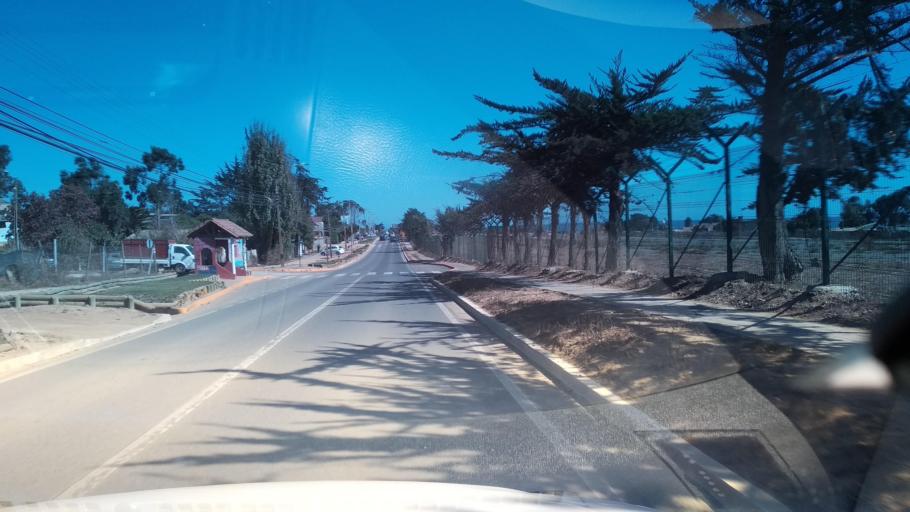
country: CL
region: O'Higgins
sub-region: Provincia de Colchagua
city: Santa Cruz
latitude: -34.3961
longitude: -72.0191
